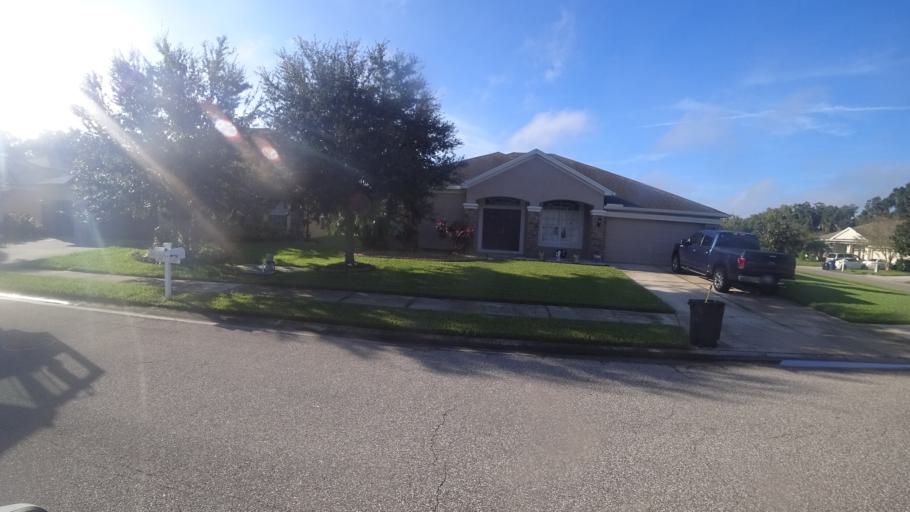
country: US
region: Florida
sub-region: Manatee County
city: Ellenton
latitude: 27.5642
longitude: -82.4654
